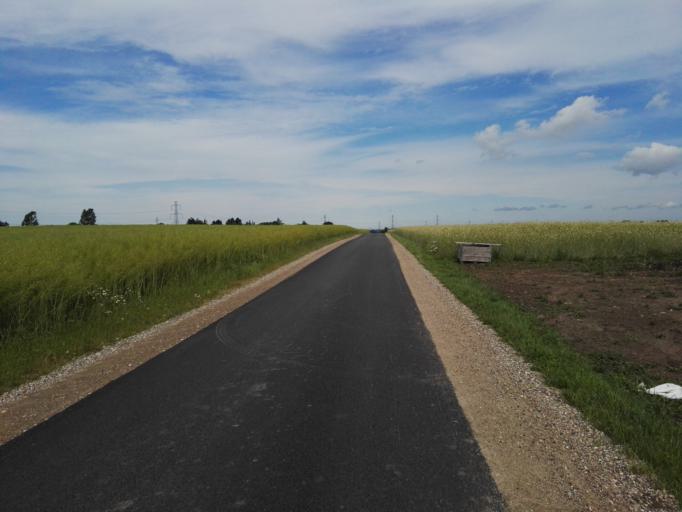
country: DK
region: Capital Region
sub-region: Egedal Kommune
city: Olstykke
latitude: 55.8199
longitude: 12.1688
